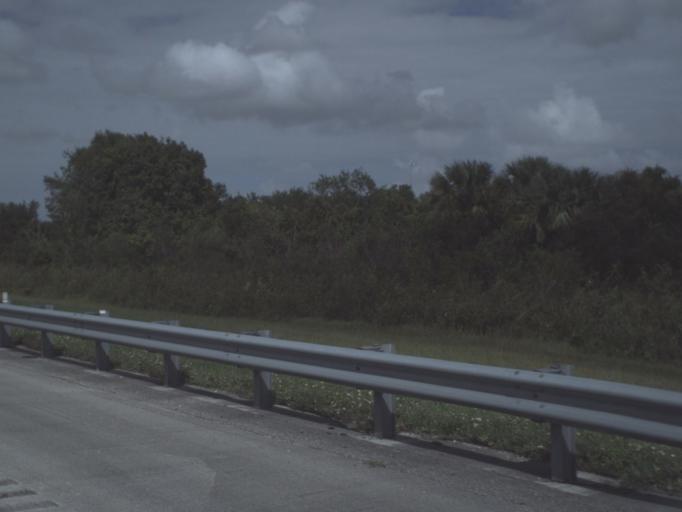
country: US
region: Florida
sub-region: Martin County
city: Hobe Sound
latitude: 27.0417
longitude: -80.2394
